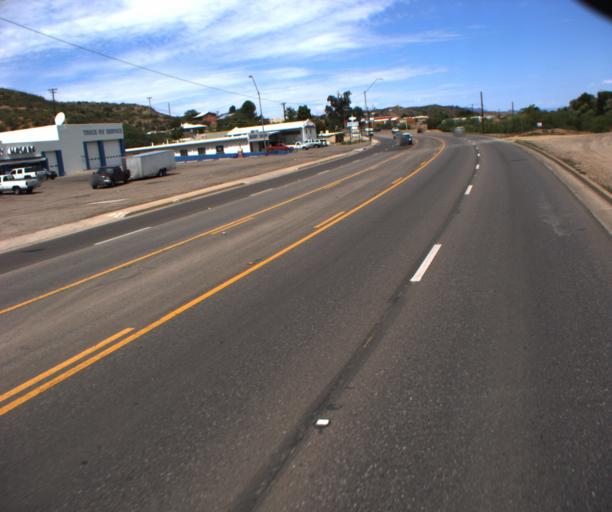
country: US
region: Arizona
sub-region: Gila County
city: Central Heights-Midland City
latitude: 33.4132
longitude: -110.7966
